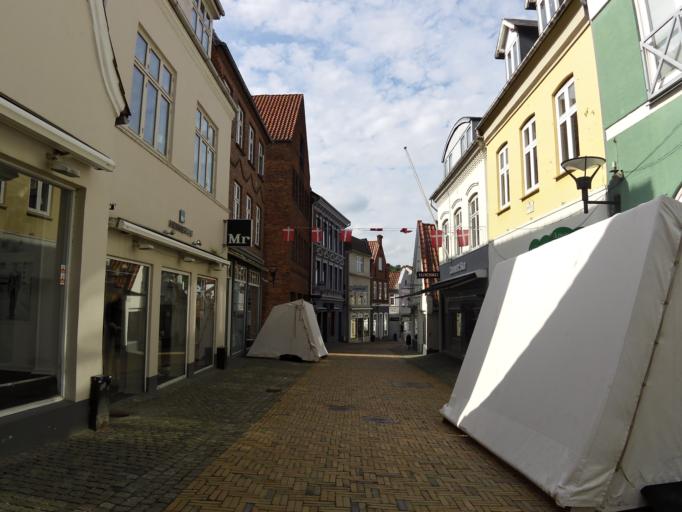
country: DK
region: South Denmark
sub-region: Aabenraa Kommune
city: Aabenraa
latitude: 55.0464
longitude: 9.4183
